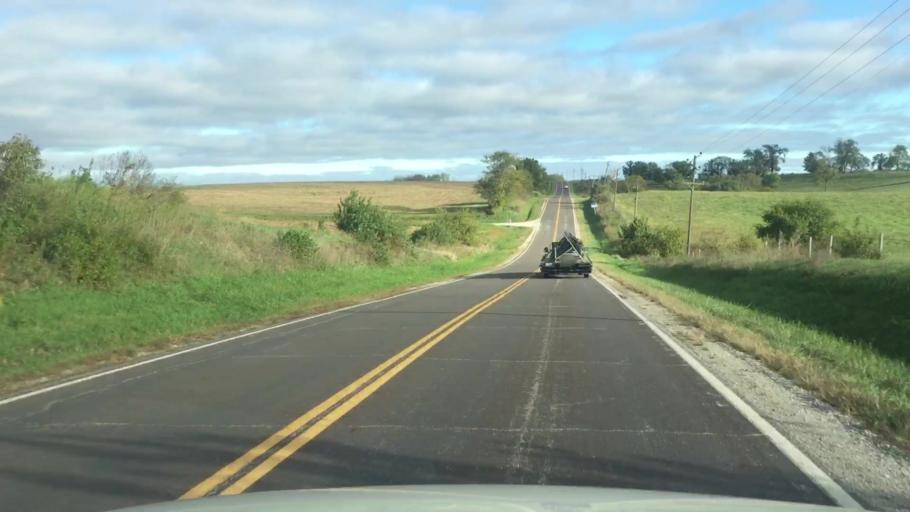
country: US
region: Missouri
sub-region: Howard County
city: New Franklin
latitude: 39.0774
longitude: -92.7456
